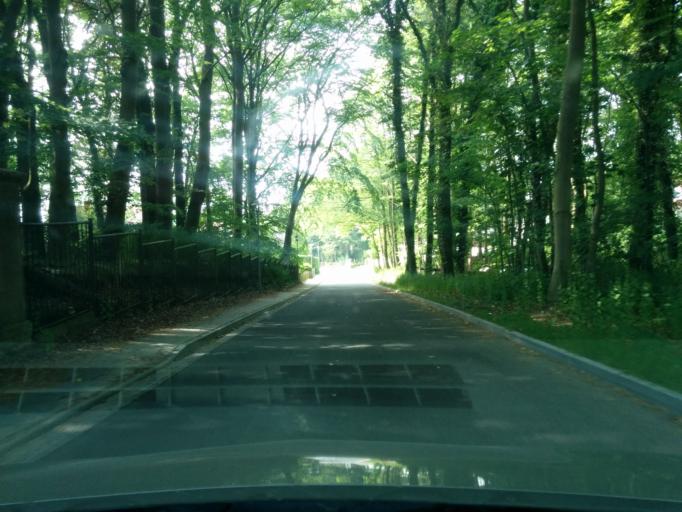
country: DE
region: Mecklenburg-Vorpommern
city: Ostseebad Zinnowitz
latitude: 54.0743
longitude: 13.9176
